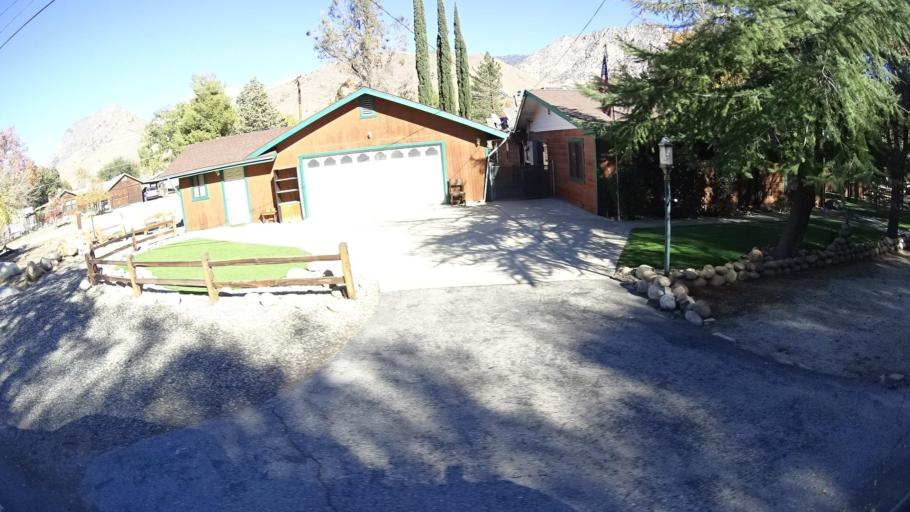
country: US
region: California
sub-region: Kern County
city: Kernville
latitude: 35.7734
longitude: -118.4424
